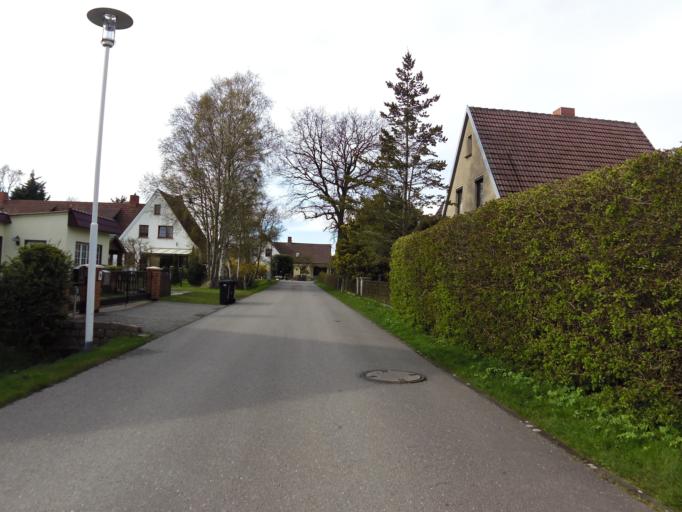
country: DE
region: Mecklenburg-Vorpommern
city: Zingst
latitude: 54.4333
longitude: 12.6768
